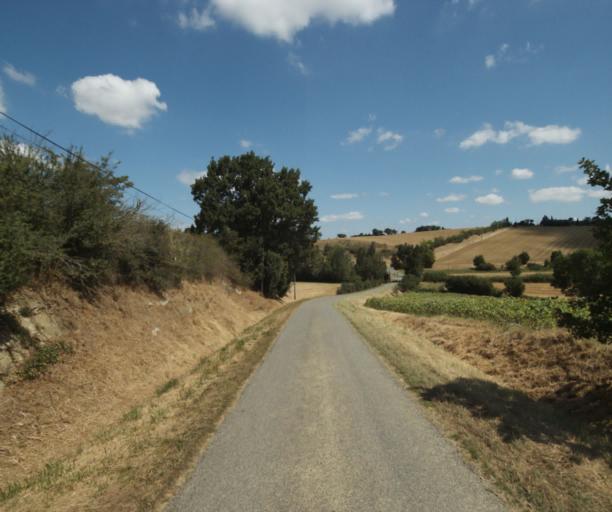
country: FR
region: Midi-Pyrenees
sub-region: Departement de la Haute-Garonne
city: Auriac-sur-Vendinelle
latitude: 43.4757
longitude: 1.8069
